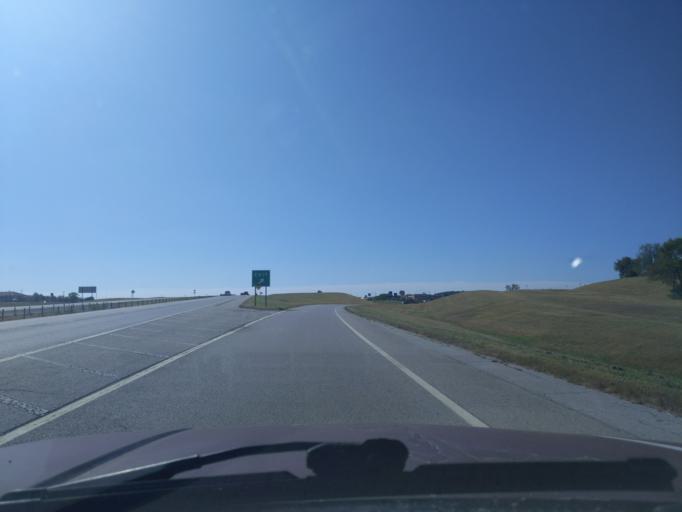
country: US
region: Oklahoma
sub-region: Tulsa County
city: Glenpool
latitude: 35.9917
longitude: -96.0119
